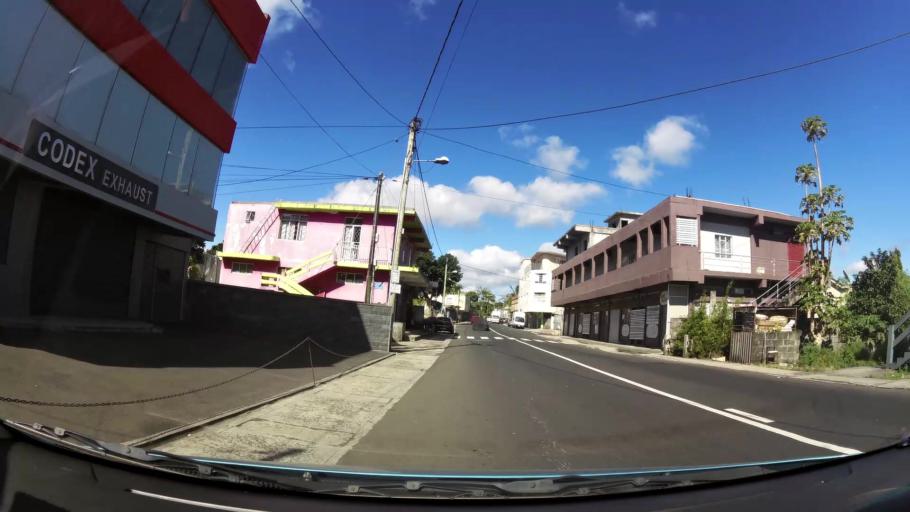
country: MU
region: Plaines Wilhems
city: Vacoas
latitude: -20.3040
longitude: 57.4924
